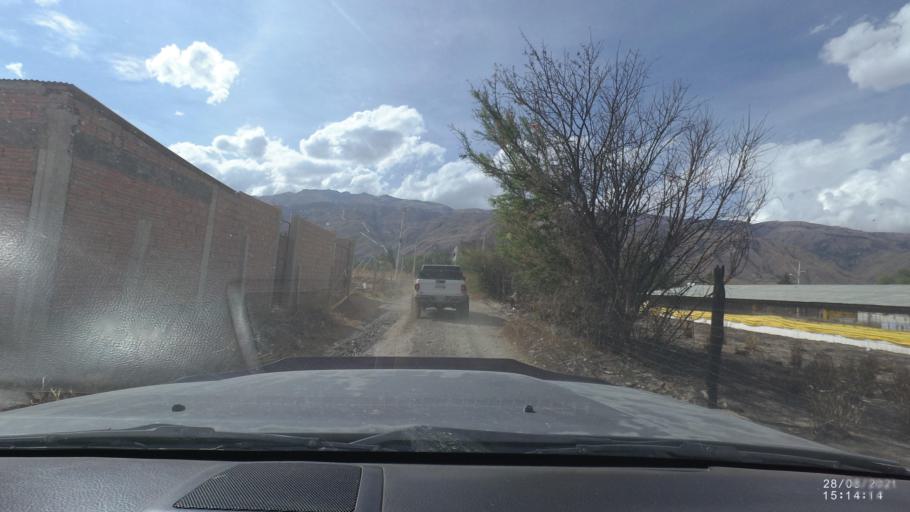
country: BO
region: Cochabamba
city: Cochabamba
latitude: -17.3369
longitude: -66.2583
